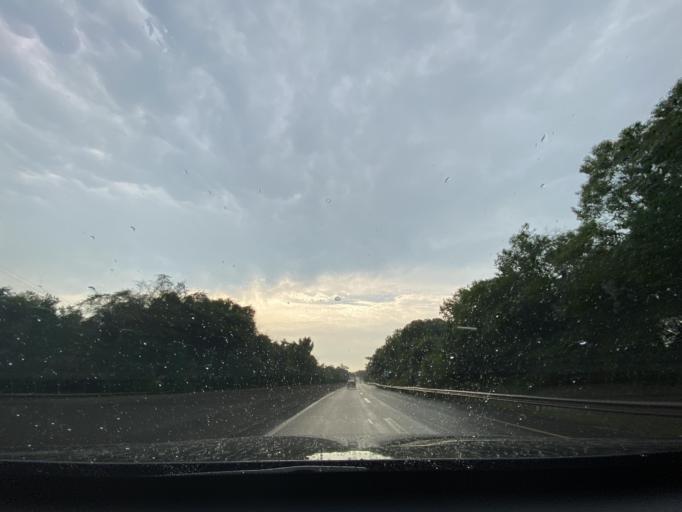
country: CN
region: Sichuan
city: Chonglong
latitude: 29.7714
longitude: 104.7562
